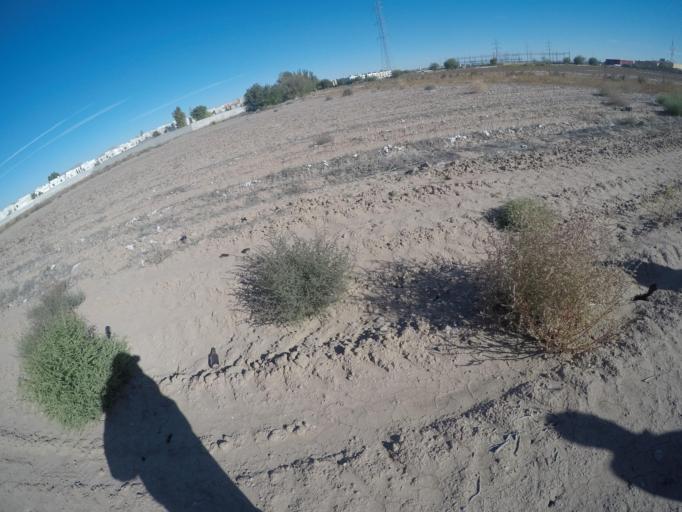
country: US
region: Texas
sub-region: El Paso County
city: Socorro
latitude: 31.6984
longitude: -106.3769
